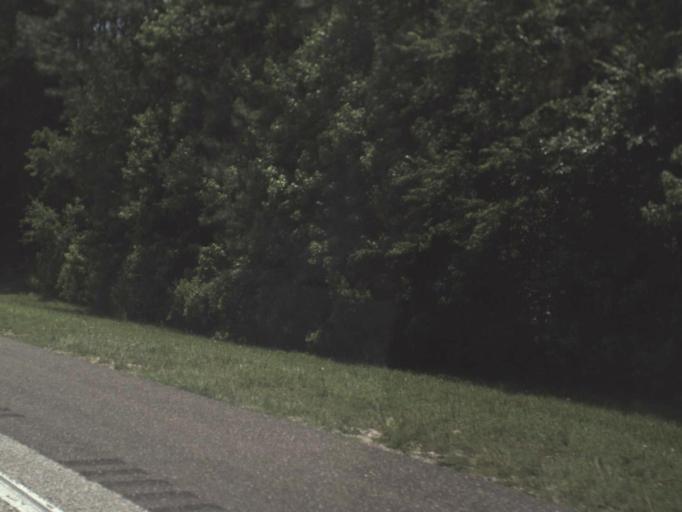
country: US
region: Florida
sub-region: Saint Johns County
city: Fruit Cove
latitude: 30.1474
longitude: -81.5451
